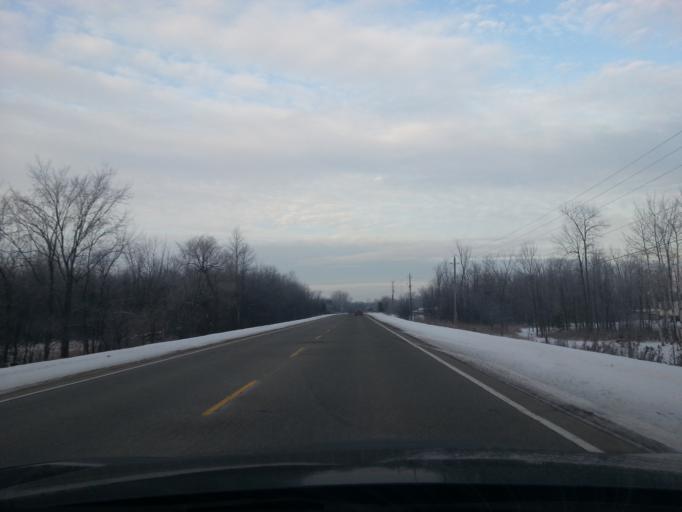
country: CA
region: Ontario
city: Carleton Place
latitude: 45.1250
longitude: -76.1538
